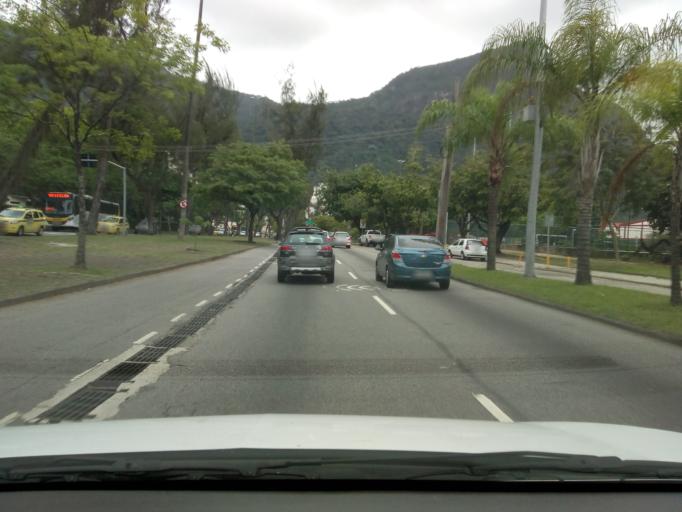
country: BR
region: Rio de Janeiro
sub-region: Rio De Janeiro
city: Rio de Janeiro
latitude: -22.9704
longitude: -43.2174
